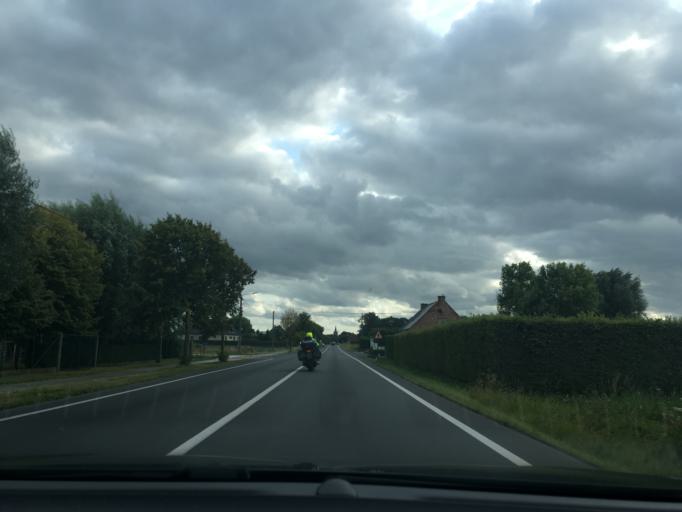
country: BE
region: Flanders
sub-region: Provincie West-Vlaanderen
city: Staden
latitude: 50.9409
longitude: 3.0264
